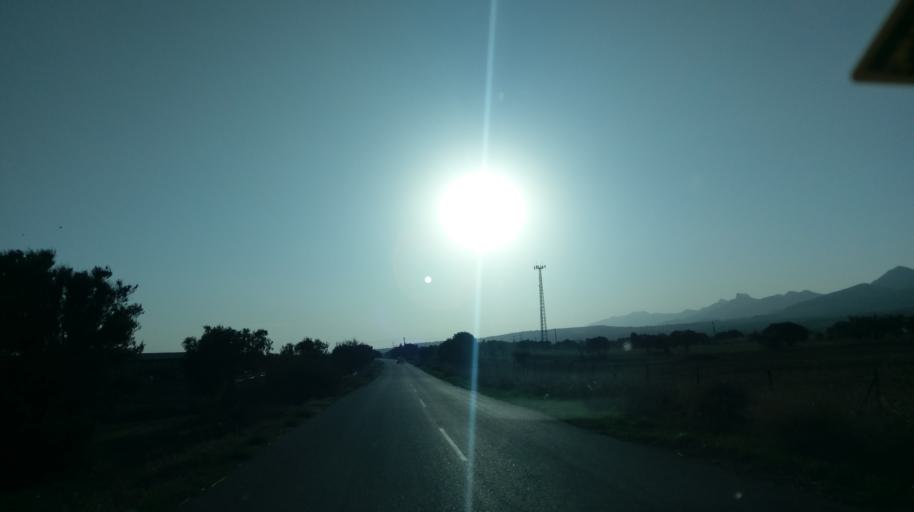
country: CY
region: Ammochostos
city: Leonarisso
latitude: 35.4242
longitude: 34.0092
